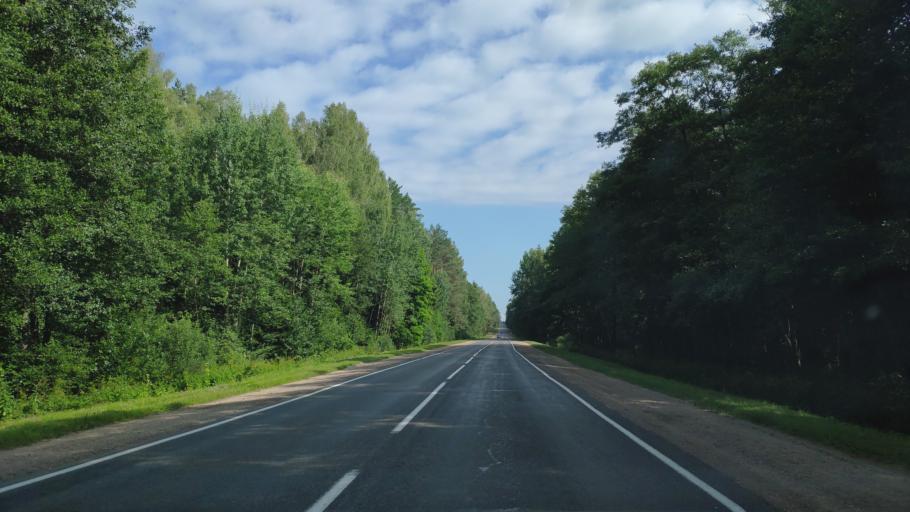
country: BY
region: Minsk
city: Novosel'ye
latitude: 53.9322
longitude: 27.2435
